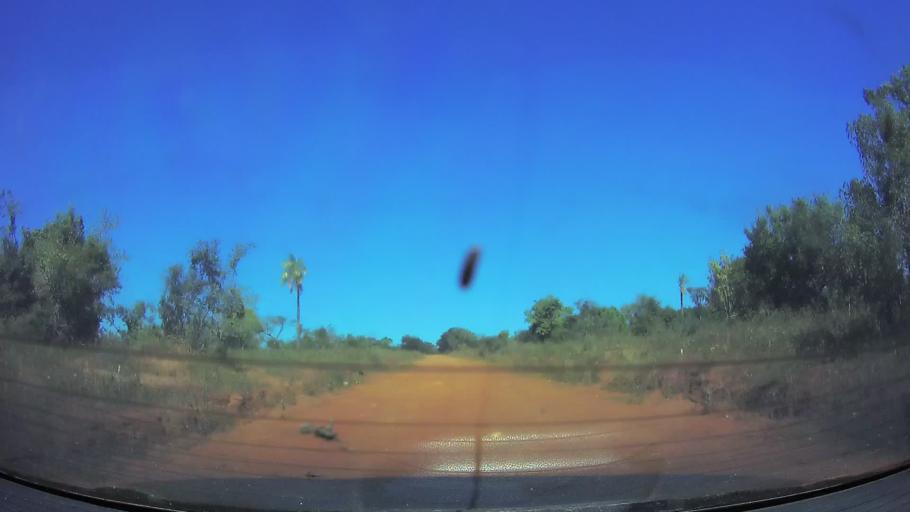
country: PY
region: Central
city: Limpio
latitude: -25.2390
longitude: -57.4517
